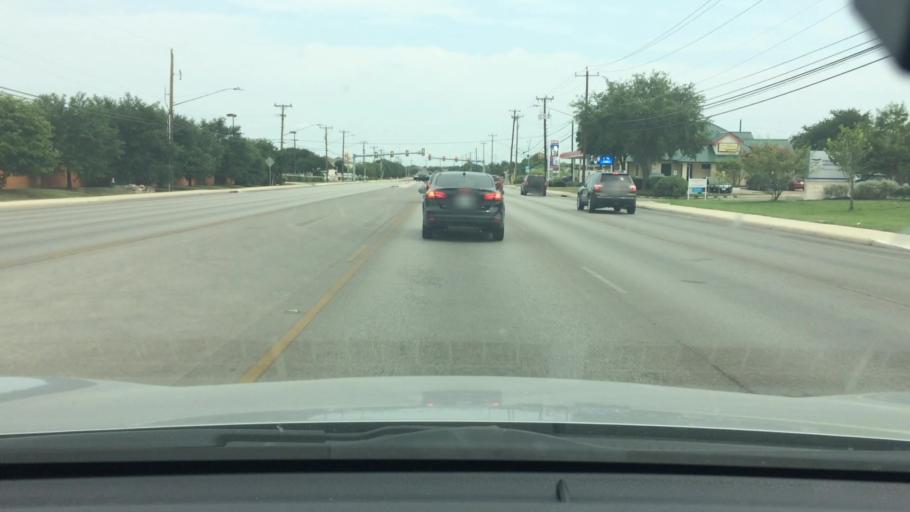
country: US
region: Texas
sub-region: Bexar County
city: Leon Valley
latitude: 29.4791
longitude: -98.6652
